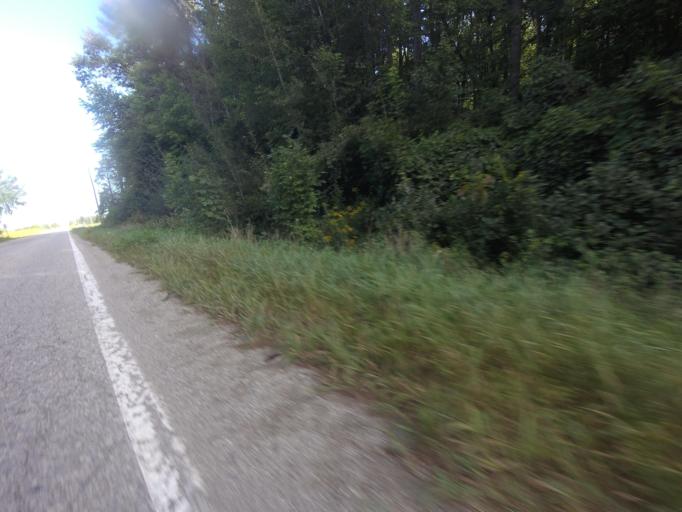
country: CA
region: Ontario
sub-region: Wellington County
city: Guelph
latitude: 43.6167
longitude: -80.3689
